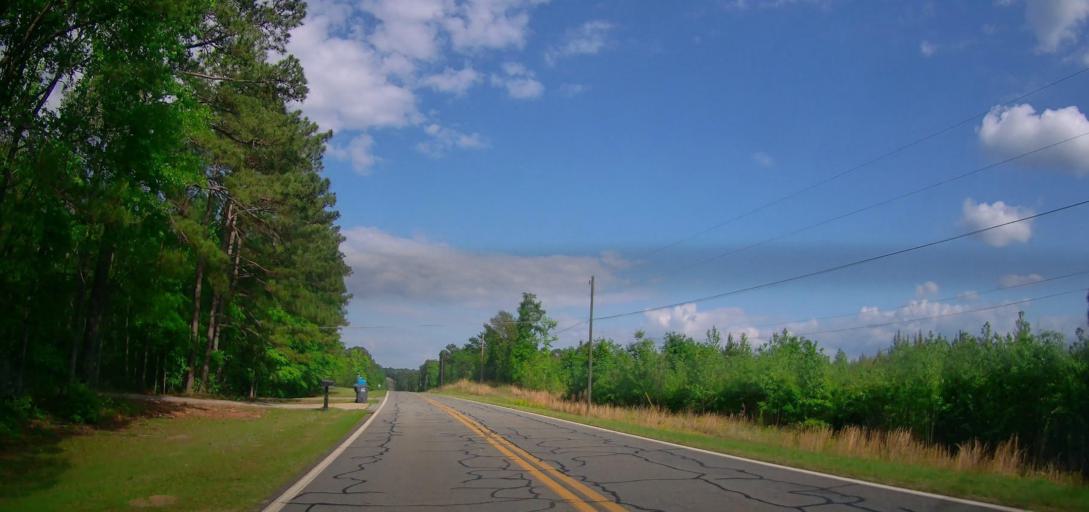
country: US
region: Georgia
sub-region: Baldwin County
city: Hardwick
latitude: 33.0641
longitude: -83.1681
